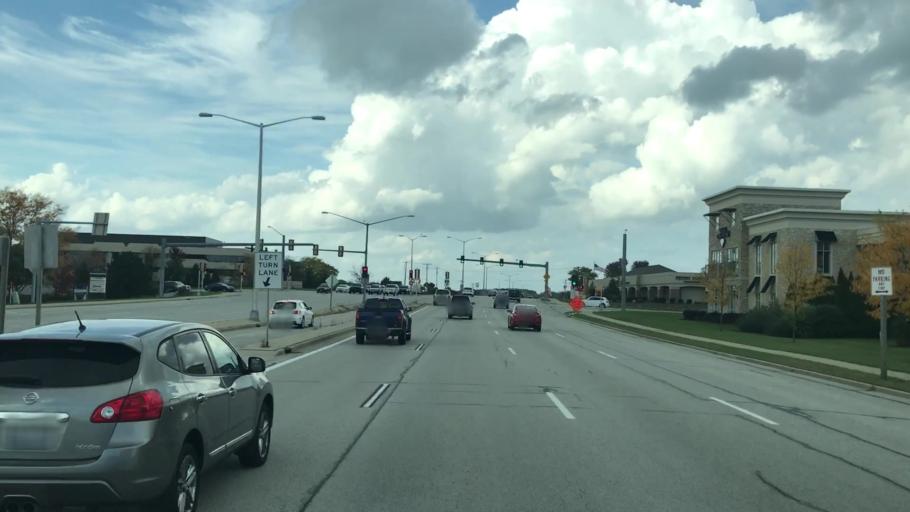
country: US
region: Wisconsin
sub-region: Waukesha County
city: Brookfield
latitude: 43.0363
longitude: -88.1128
